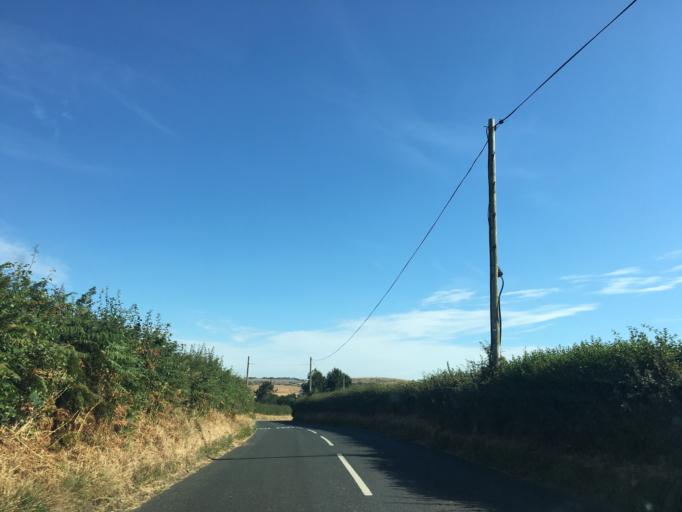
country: GB
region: England
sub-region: Isle of Wight
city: Chale
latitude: 50.6257
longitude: -1.3207
